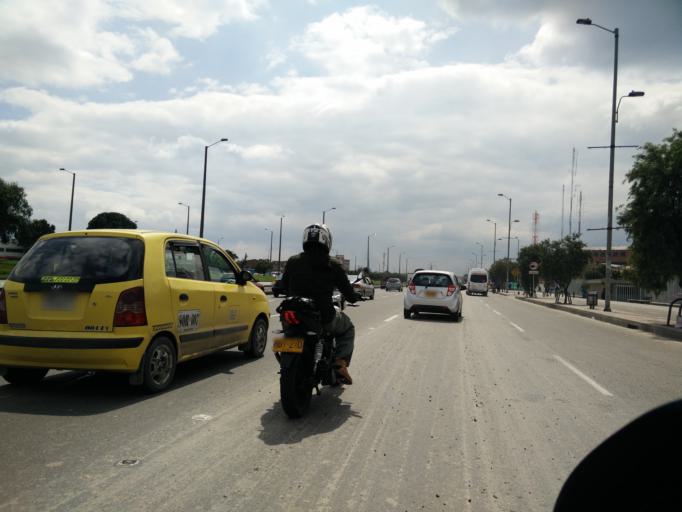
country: CO
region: Bogota D.C.
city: Bogota
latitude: 4.6284
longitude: -74.1124
